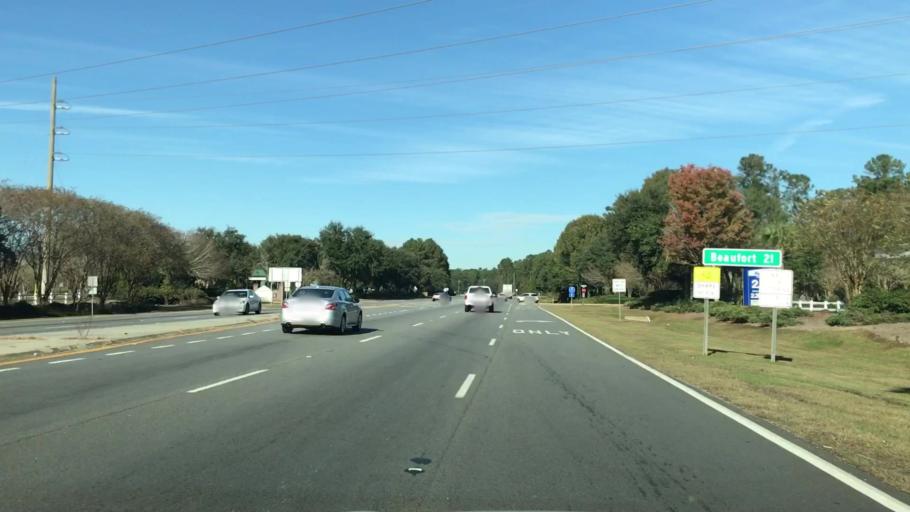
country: US
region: South Carolina
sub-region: Beaufort County
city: Bluffton
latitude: 32.2955
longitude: -80.9362
